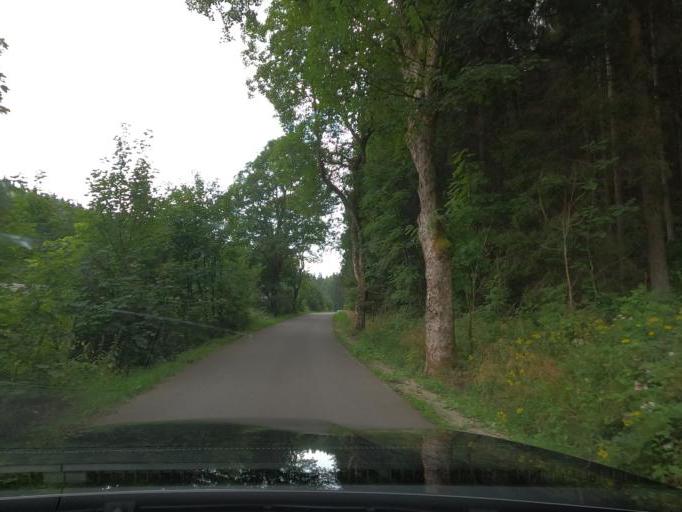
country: DE
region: Lower Saxony
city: Wildemann
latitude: 51.7926
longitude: 10.3004
